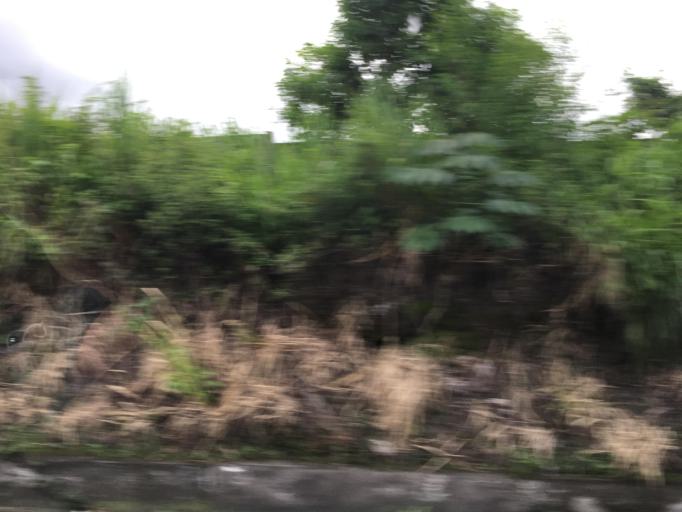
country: GT
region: Escuintla
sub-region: Municipio de Escuintla
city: Escuintla
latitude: 14.3848
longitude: -90.8268
